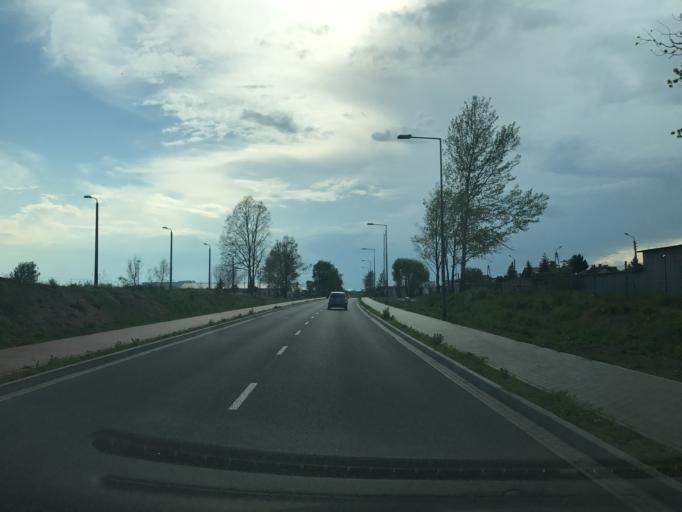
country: PL
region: Kujawsko-Pomorskie
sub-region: Powiat swiecki
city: Swiecie
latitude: 53.4040
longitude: 18.4272
